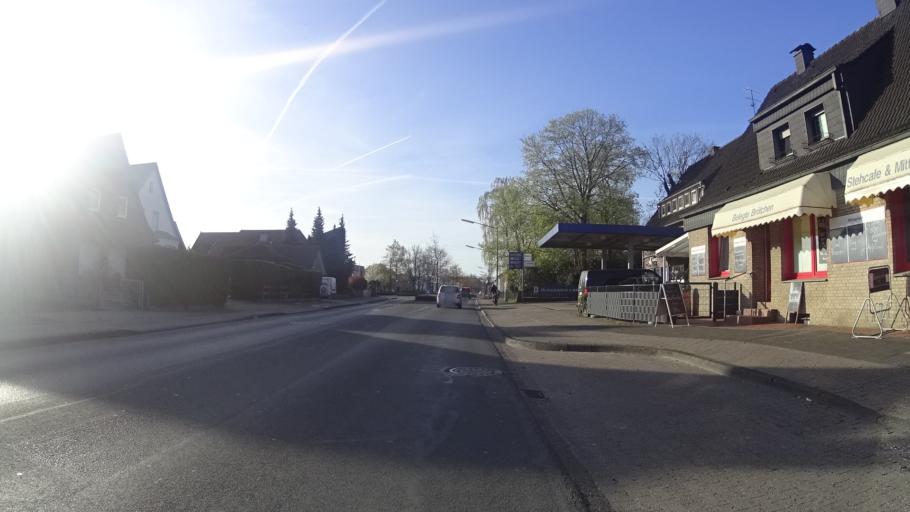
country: DE
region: North Rhine-Westphalia
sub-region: Regierungsbezirk Munster
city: Greven
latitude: 52.1260
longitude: 7.5524
